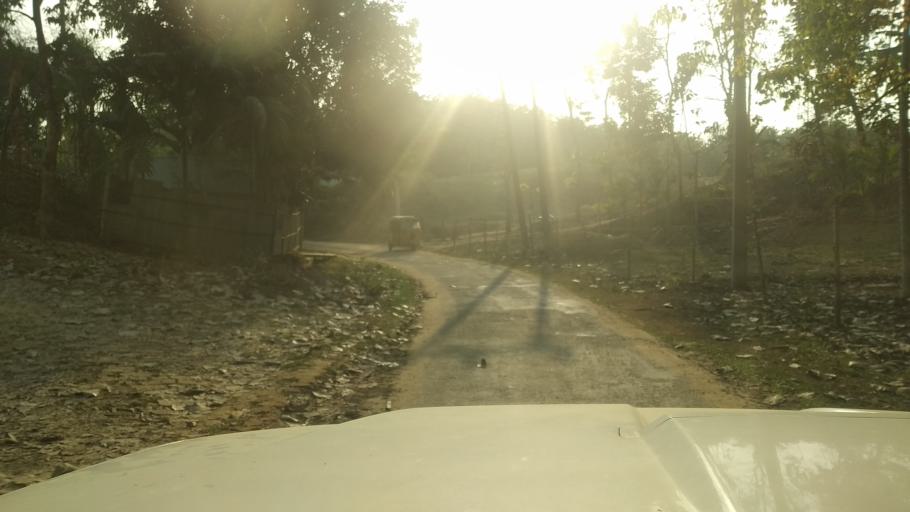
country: IN
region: Tripura
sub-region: West Tripura
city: Sonamura
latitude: 23.3494
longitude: 91.3227
